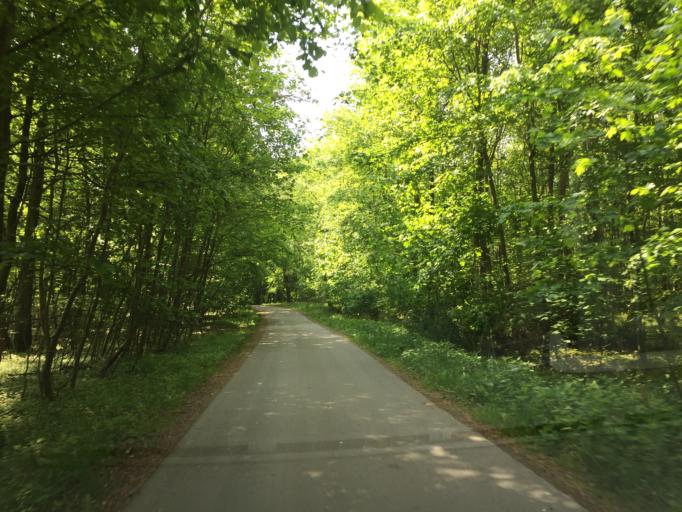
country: DK
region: South Denmark
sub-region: Langeland Kommune
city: Rudkobing
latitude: 54.9849
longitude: 10.8047
